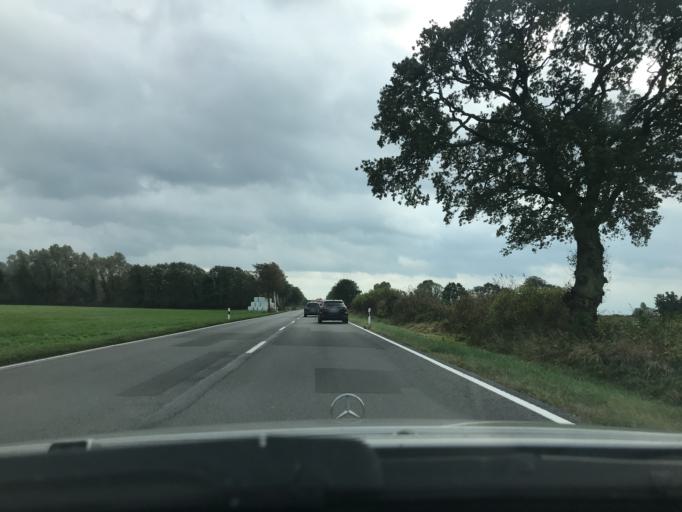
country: DE
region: Mecklenburg-Vorpommern
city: Koserow
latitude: 54.0526
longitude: 13.9910
